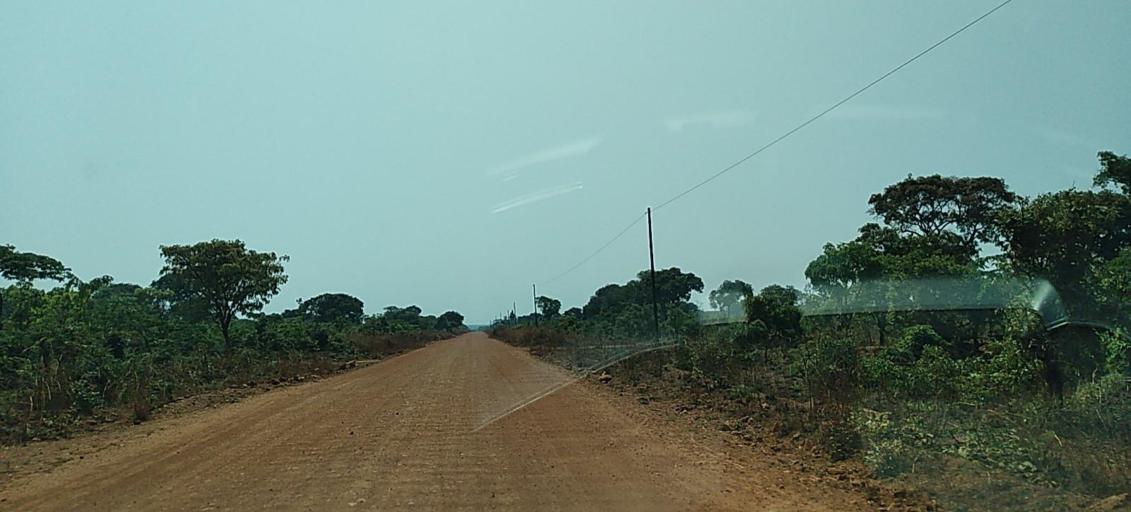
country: ZM
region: North-Western
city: Kansanshi
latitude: -11.9967
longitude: 26.5995
